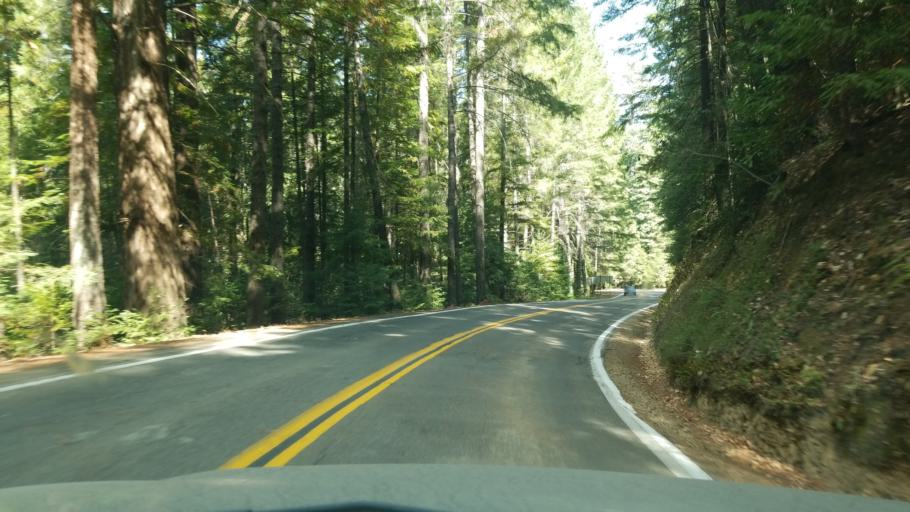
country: US
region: California
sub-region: Humboldt County
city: Redway
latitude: 39.8561
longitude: -123.7173
